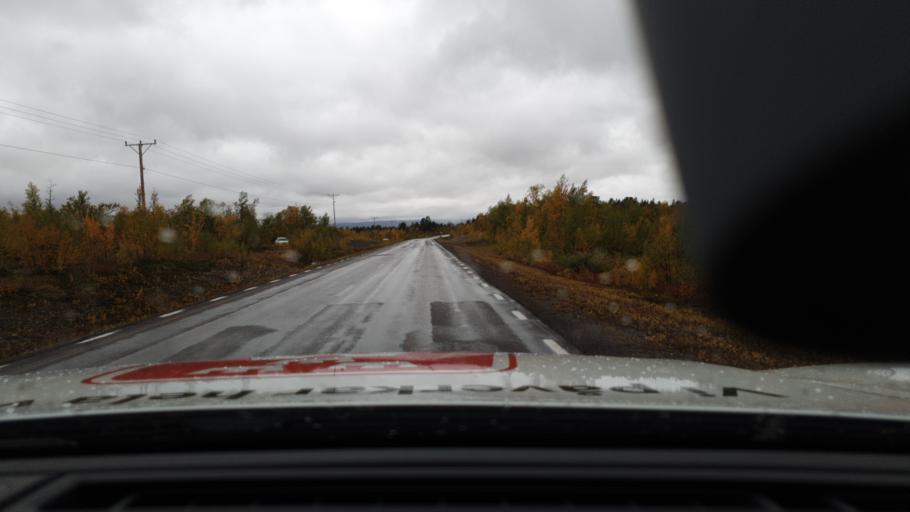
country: SE
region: Norrbotten
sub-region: Kiruna Kommun
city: Kiruna
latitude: 67.7654
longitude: 20.1437
